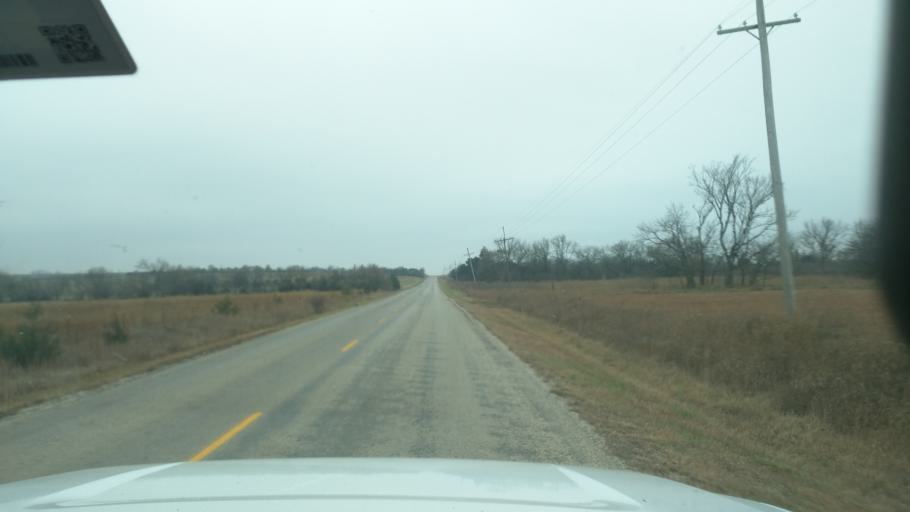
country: US
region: Kansas
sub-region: Lyon County
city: Emporia
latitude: 38.5740
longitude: -96.2611
